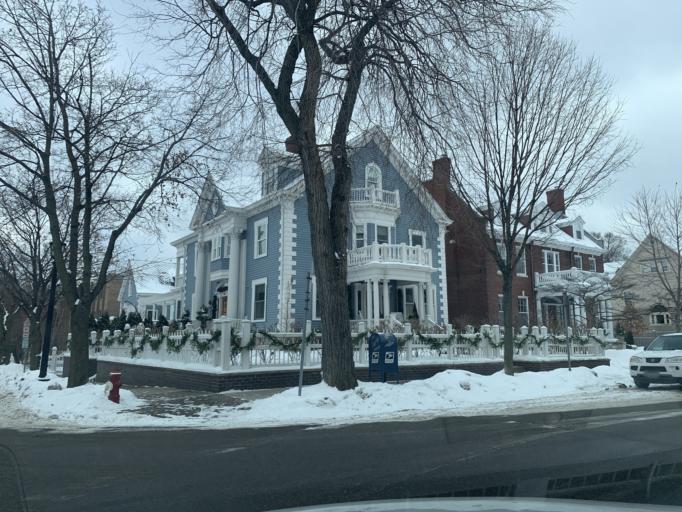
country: US
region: Minnesota
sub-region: Hennepin County
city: Minneapolis
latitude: 44.9664
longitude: -93.2919
